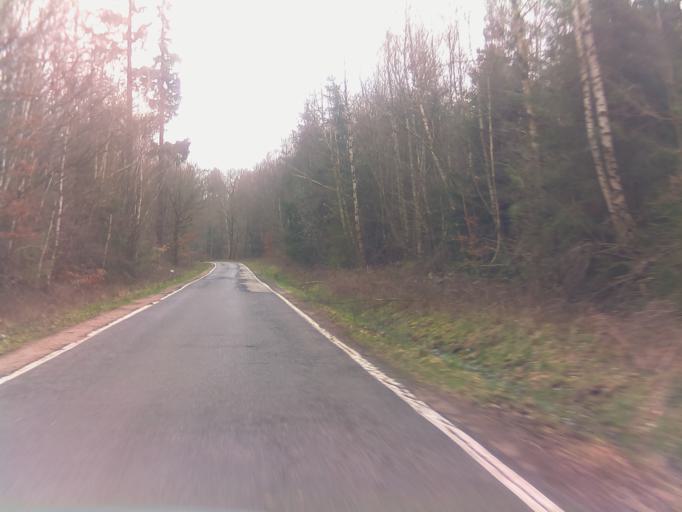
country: DE
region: Rheinland-Pfalz
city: Waldalgesheim
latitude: 49.9747
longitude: 7.8358
